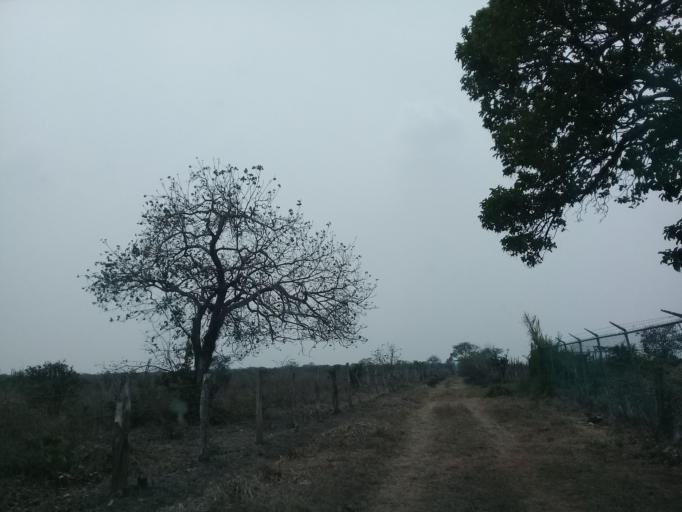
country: MX
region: Veracruz
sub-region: Medellin
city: La Laguna y Monte del Castillo
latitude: 18.9068
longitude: -96.1298
